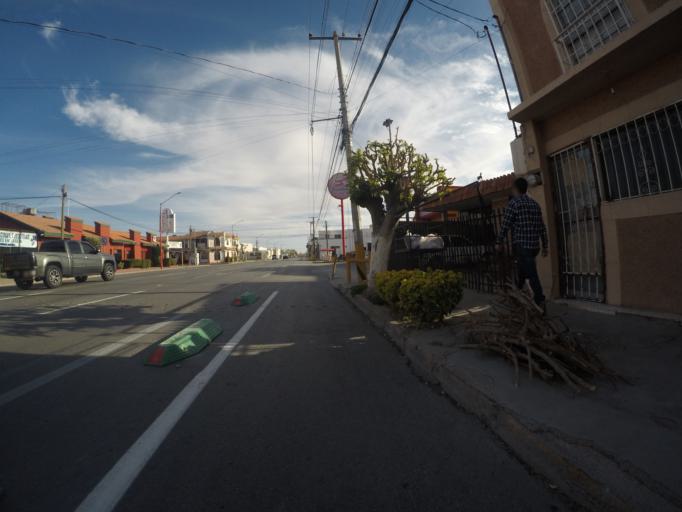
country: MX
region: Chihuahua
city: Ciudad Juarez
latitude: 31.7511
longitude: -106.4484
